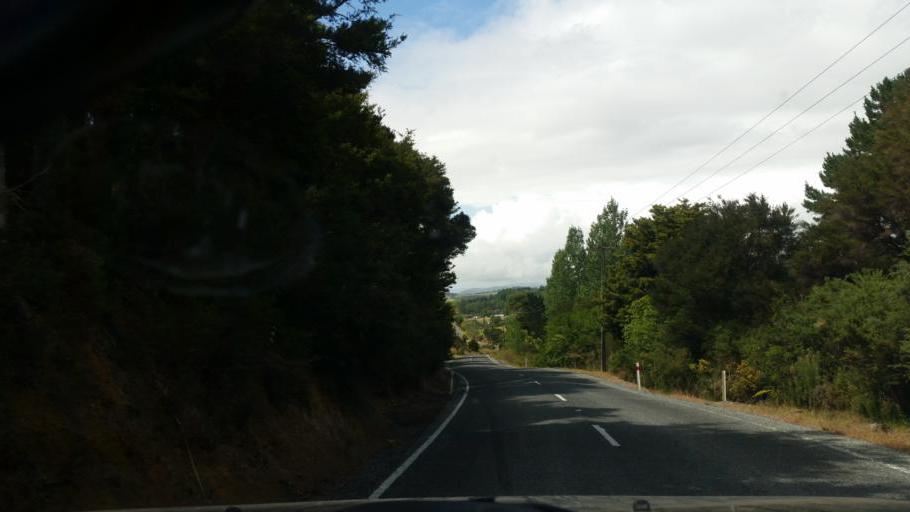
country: NZ
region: Auckland
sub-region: Auckland
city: Wellsford
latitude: -36.1149
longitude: 174.5434
